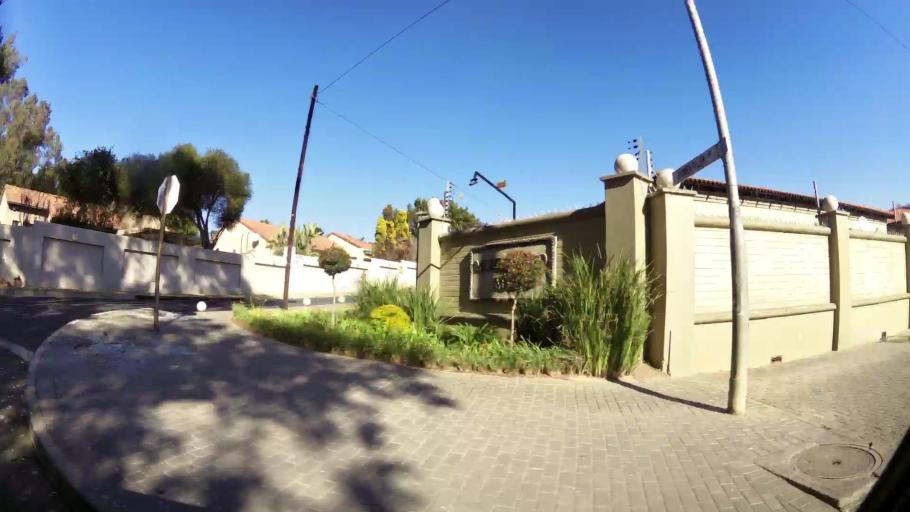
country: ZA
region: Gauteng
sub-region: West Rand District Municipality
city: Muldersdriseloop
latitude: -26.0506
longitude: 27.9603
